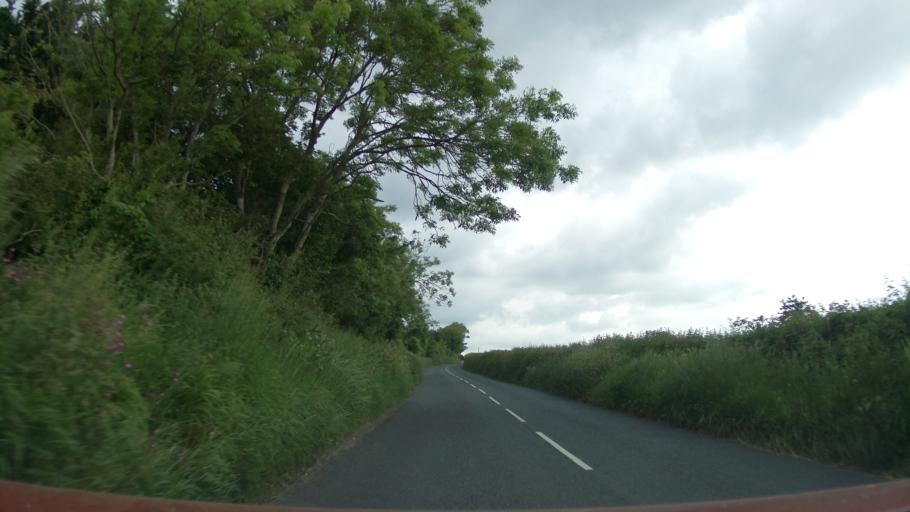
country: GB
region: England
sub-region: South Gloucestershire
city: Pucklechurch
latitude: 51.4764
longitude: -2.4270
